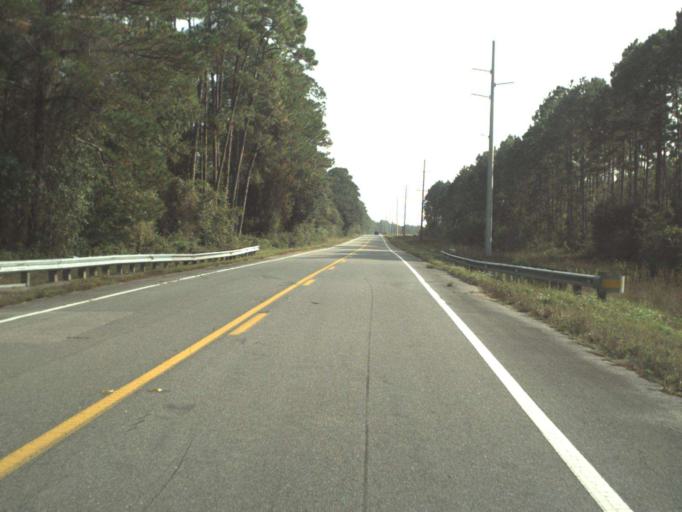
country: US
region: Florida
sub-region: Franklin County
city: Carrabelle
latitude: 29.9546
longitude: -84.5051
